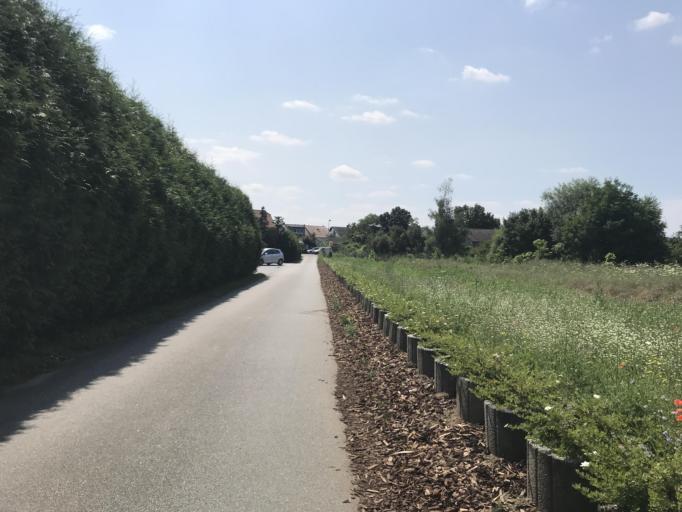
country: DE
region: Hesse
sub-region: Regierungsbezirk Darmstadt
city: Hochheim am Main
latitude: 50.0098
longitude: 8.3137
